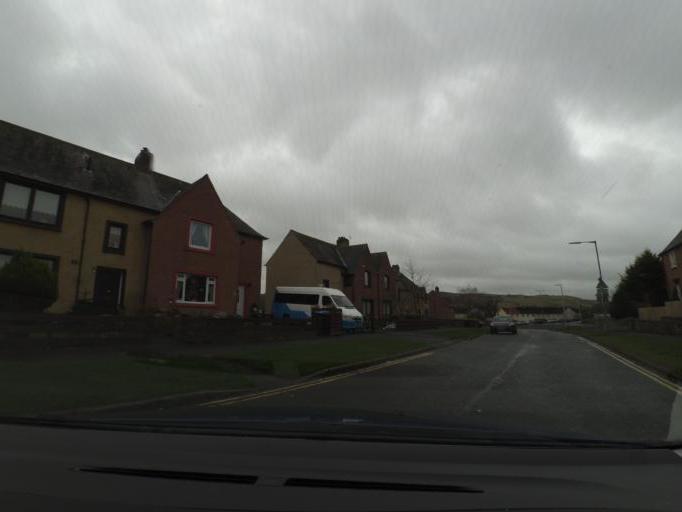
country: GB
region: Scotland
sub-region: The Scottish Borders
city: Hawick
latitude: 55.4365
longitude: -2.7687
